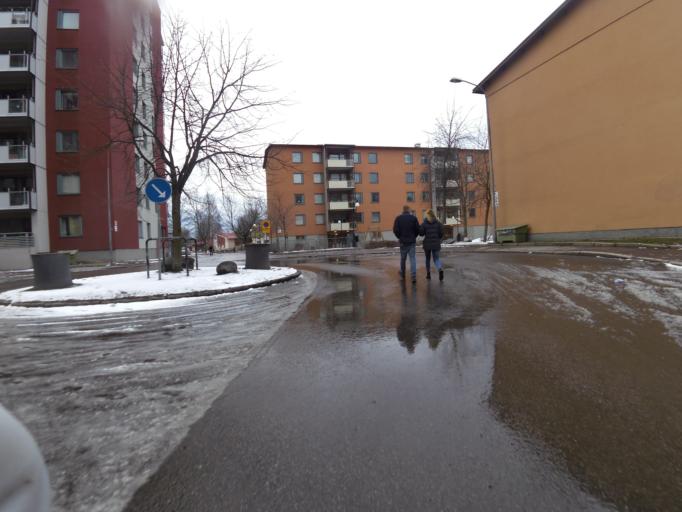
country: SE
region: Gaevleborg
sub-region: Gavle Kommun
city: Gavle
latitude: 60.6789
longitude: 17.1517
